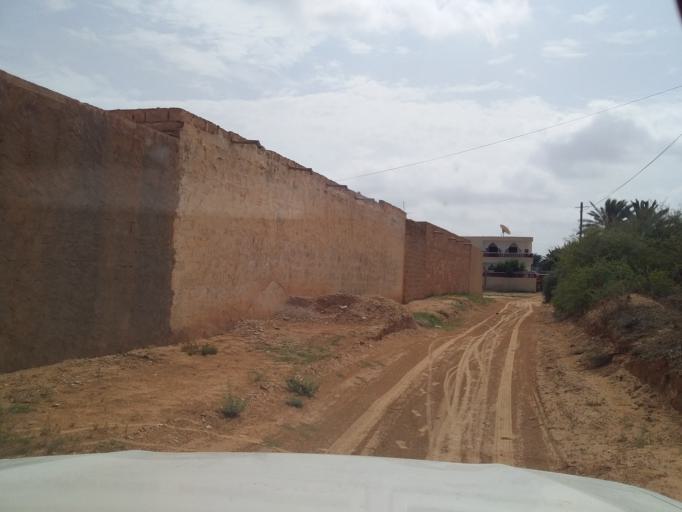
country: TN
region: Qabis
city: Gabes
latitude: 33.6282
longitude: 10.3106
